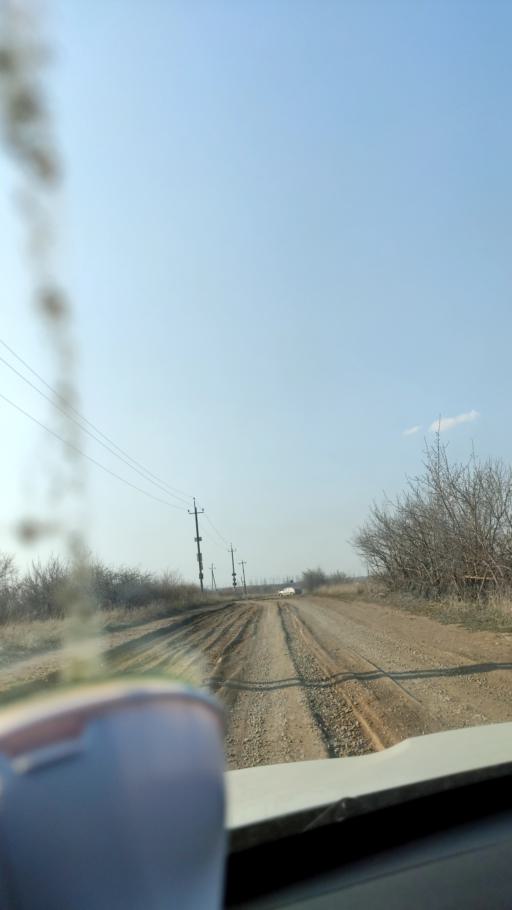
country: RU
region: Samara
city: Kinel'
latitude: 53.2535
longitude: 50.5310
